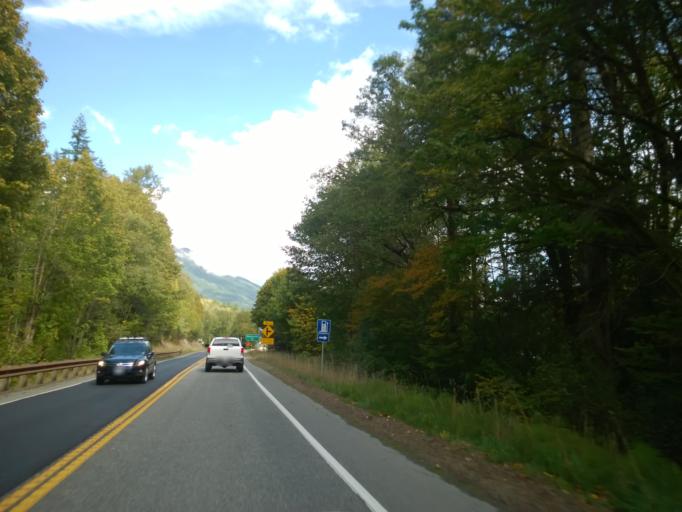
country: US
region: Washington
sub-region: Snohomish County
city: Gold Bar
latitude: 47.7107
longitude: -121.3644
